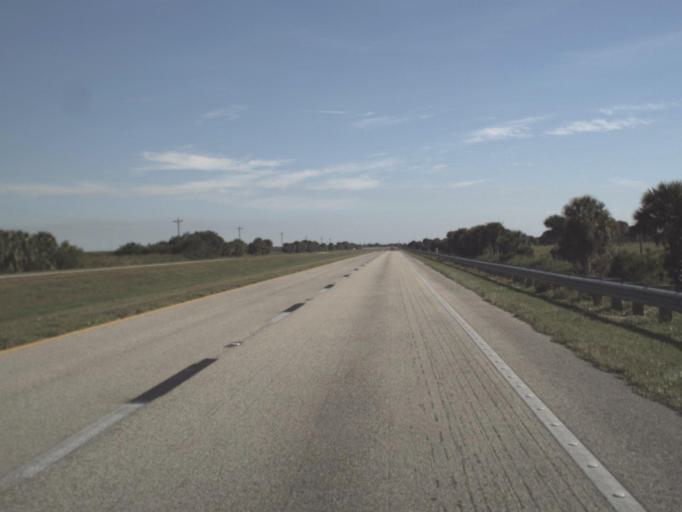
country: US
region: Florida
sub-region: Glades County
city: Moore Haven
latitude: 26.8469
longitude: -81.2011
